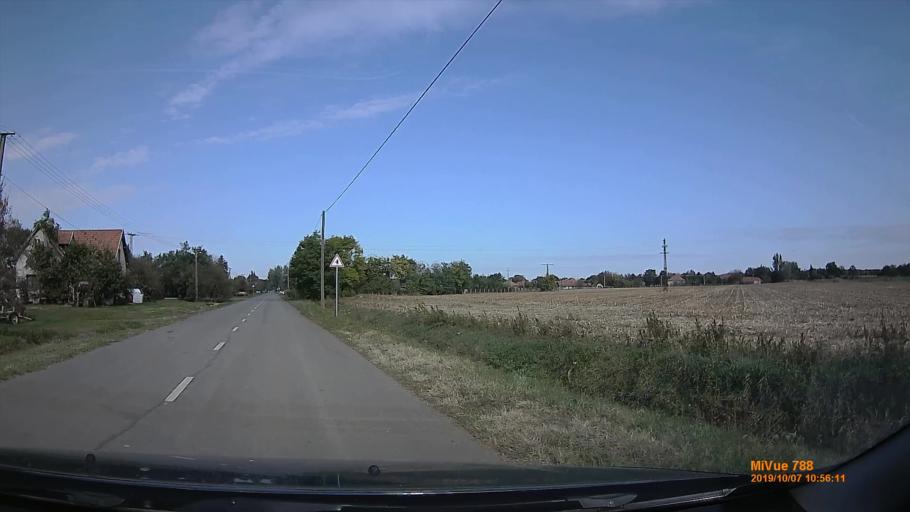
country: HU
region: Bekes
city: Kondoros
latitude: 46.7471
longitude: 20.8027
